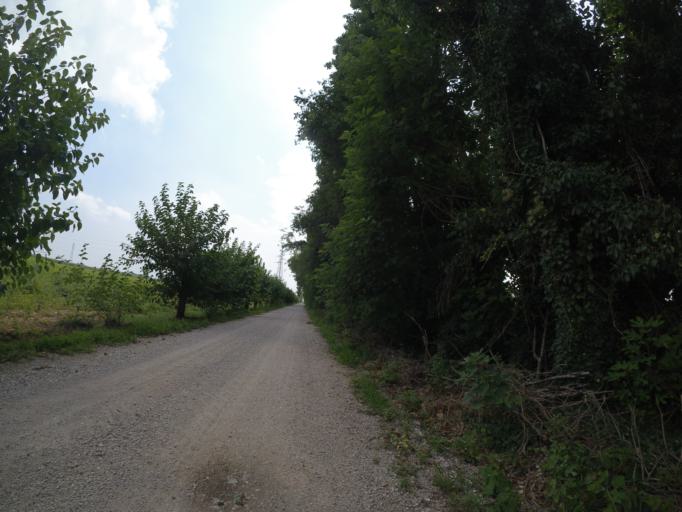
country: IT
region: Friuli Venezia Giulia
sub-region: Provincia di Udine
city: Sedegliano
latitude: 46.0032
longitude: 13.0107
